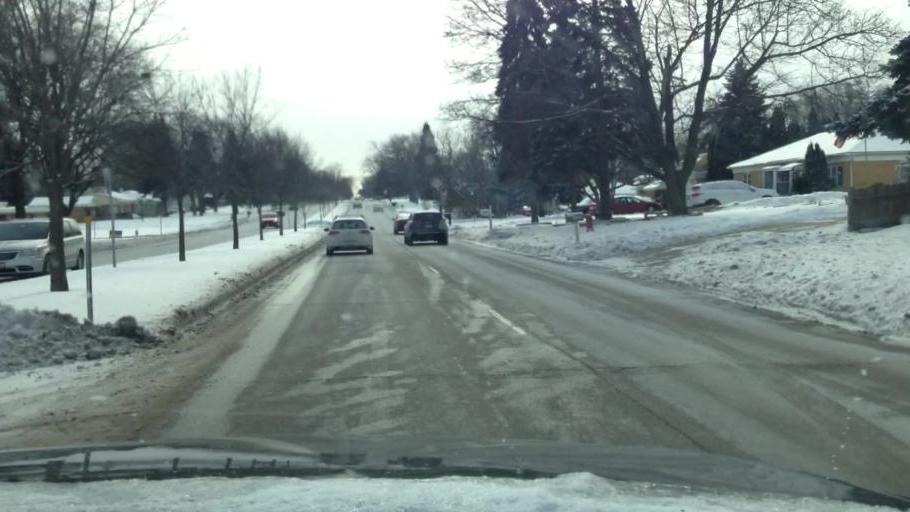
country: US
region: Illinois
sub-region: DuPage County
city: Lombard
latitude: 41.8587
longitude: -88.0123
